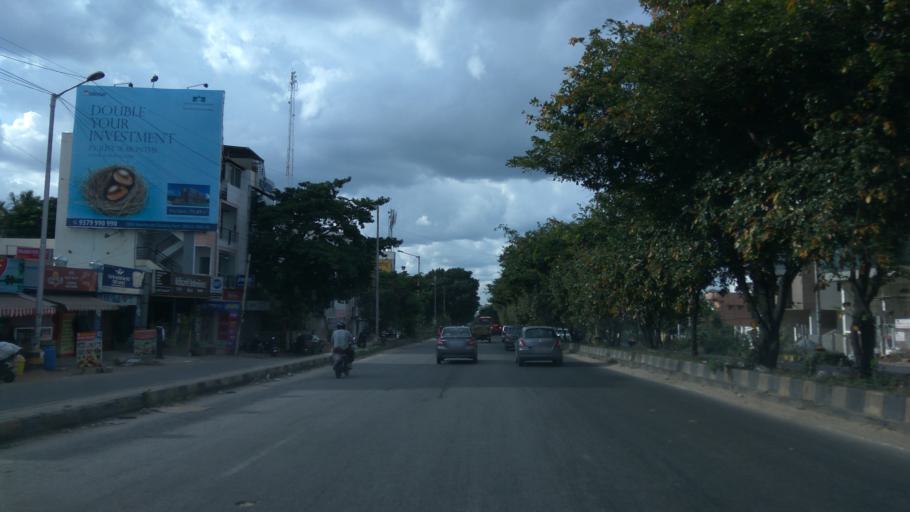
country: IN
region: Karnataka
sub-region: Bangalore Urban
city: Bangalore
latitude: 13.0295
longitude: 77.6312
